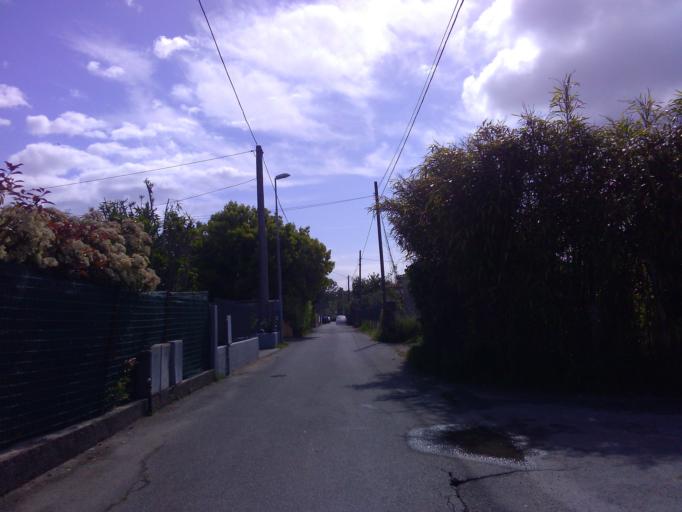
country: IT
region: Tuscany
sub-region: Provincia di Massa-Carrara
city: Marina di Carrara
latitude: 44.0480
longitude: 10.0387
